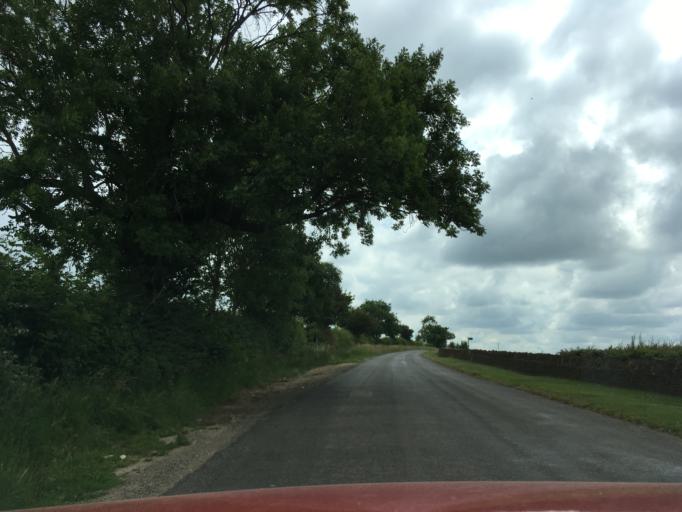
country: GB
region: England
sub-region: Oxfordshire
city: Chipping Norton
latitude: 51.9257
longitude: -1.5607
